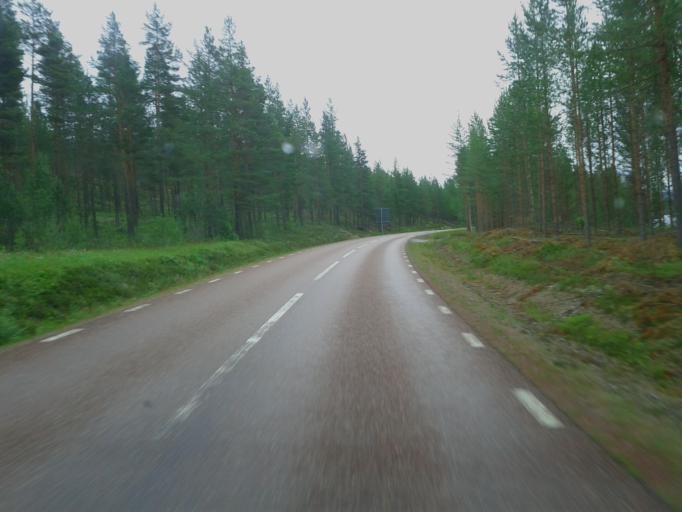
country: NO
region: Hedmark
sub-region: Trysil
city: Innbygda
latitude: 61.7943
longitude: 12.9228
